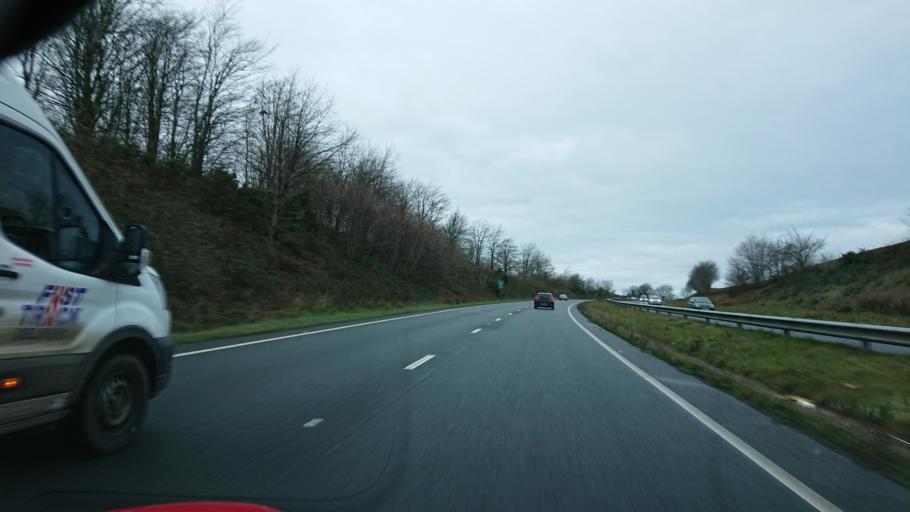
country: GB
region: England
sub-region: Cornwall
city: Liskeard
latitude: 50.4304
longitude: -4.4335
